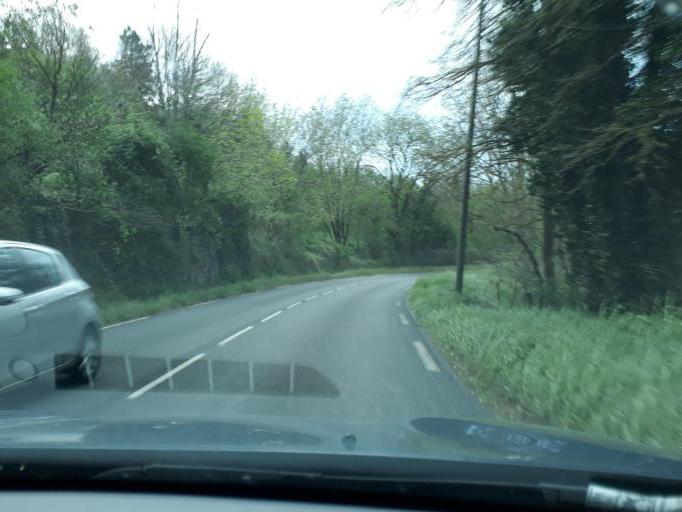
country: FR
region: Rhone-Alpes
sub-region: Departement du Rhone
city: Soucieu-en-Jarrest
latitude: 45.6762
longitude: 4.7068
